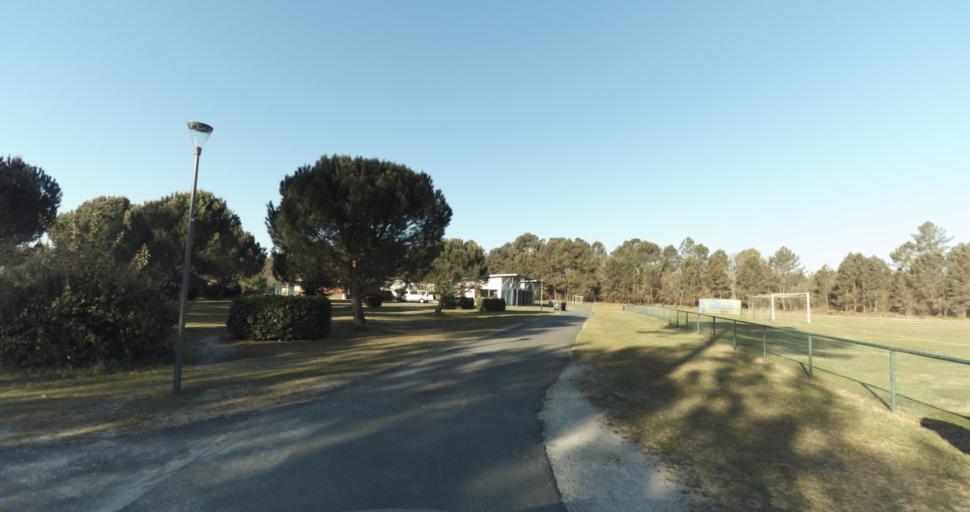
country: FR
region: Aquitaine
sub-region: Departement de la Gironde
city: Martignas-sur-Jalle
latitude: 44.8086
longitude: -0.7987
